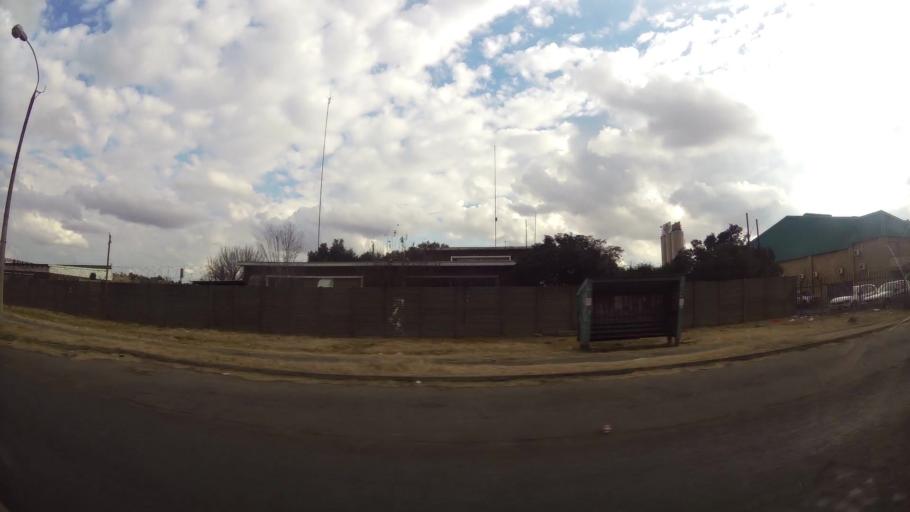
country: ZA
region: Orange Free State
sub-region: Fezile Dabi District Municipality
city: Sasolburg
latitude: -26.8236
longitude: 27.8360
